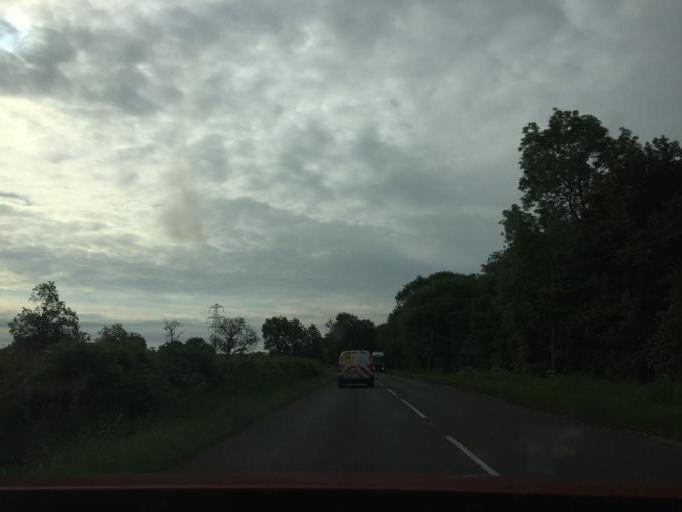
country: GB
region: England
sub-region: Leicestershire
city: Sapcote
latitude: 52.4612
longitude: -1.2936
